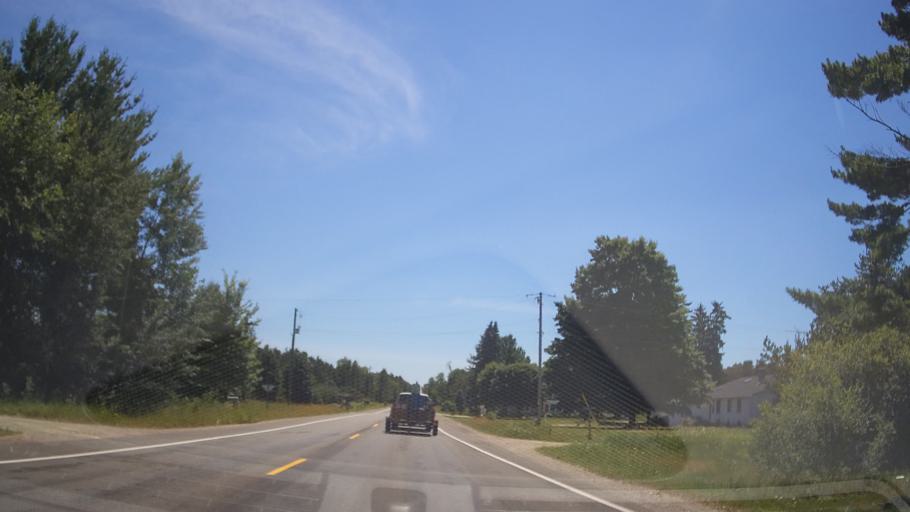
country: US
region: Michigan
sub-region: Grand Traverse County
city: Traverse City
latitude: 44.6430
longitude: -85.6964
